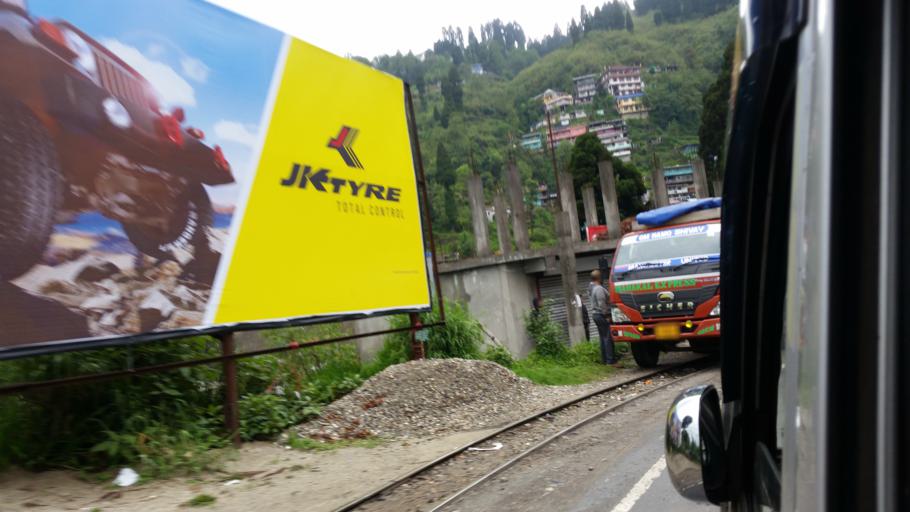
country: IN
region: West Bengal
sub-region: Darjiling
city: Darjiling
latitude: 27.0204
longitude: 88.2520
